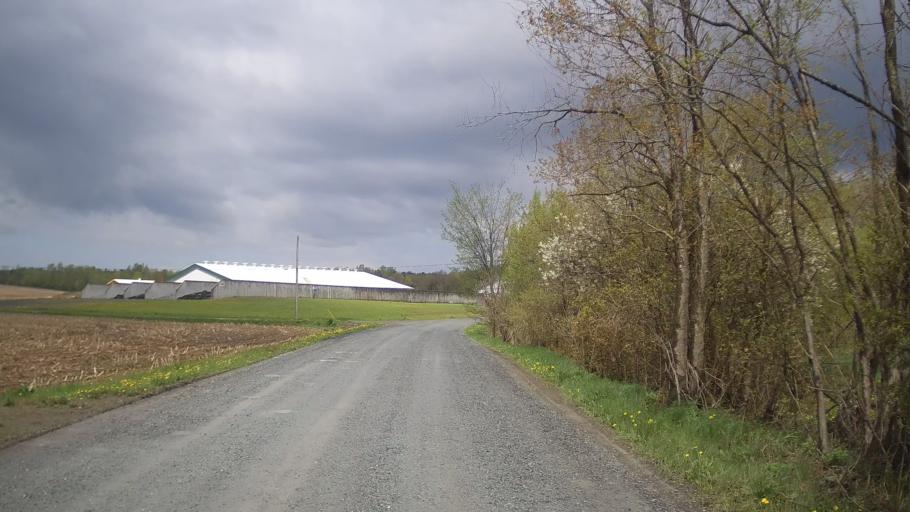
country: CA
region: Quebec
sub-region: Monteregie
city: Cowansville
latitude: 45.1749
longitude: -72.6884
